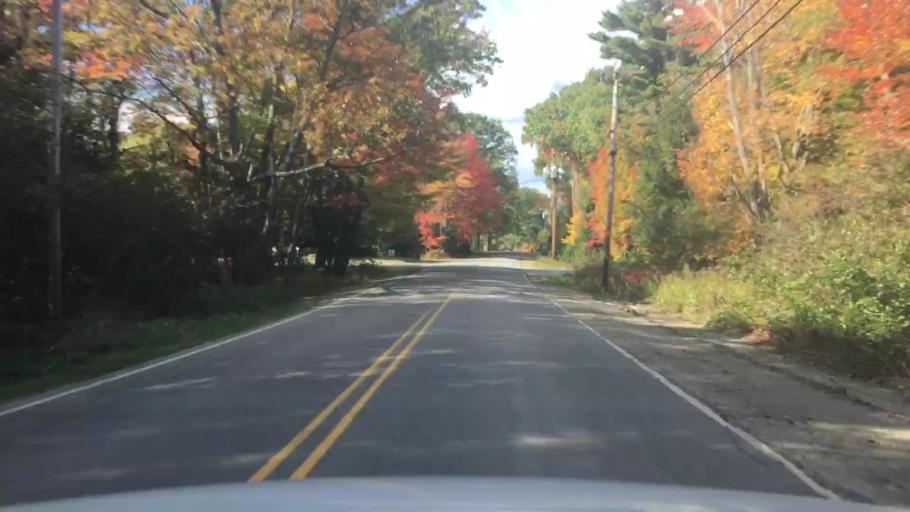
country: US
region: Maine
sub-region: Knox County
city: Warren
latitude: 44.1478
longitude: -69.2357
